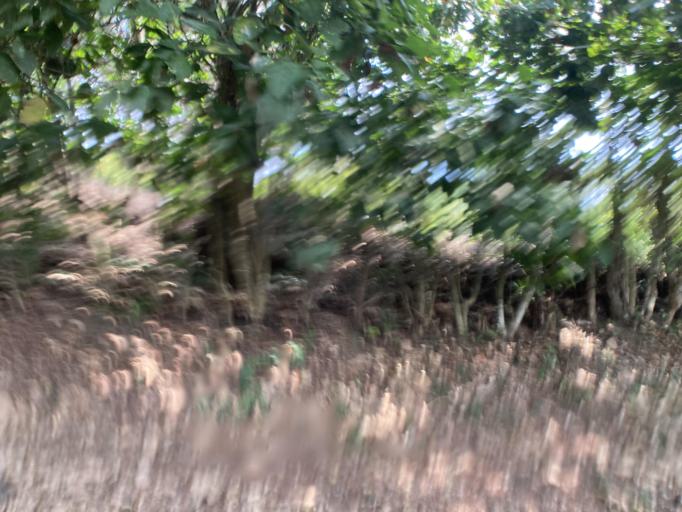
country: GT
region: Escuintla
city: San Vicente Pacaya
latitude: 14.3861
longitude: -90.5525
